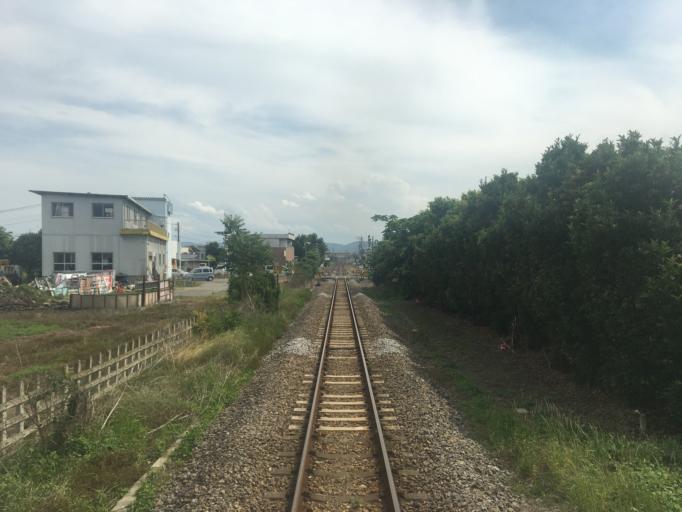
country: JP
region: Gunma
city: Fujioka
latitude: 36.2561
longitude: 139.0835
